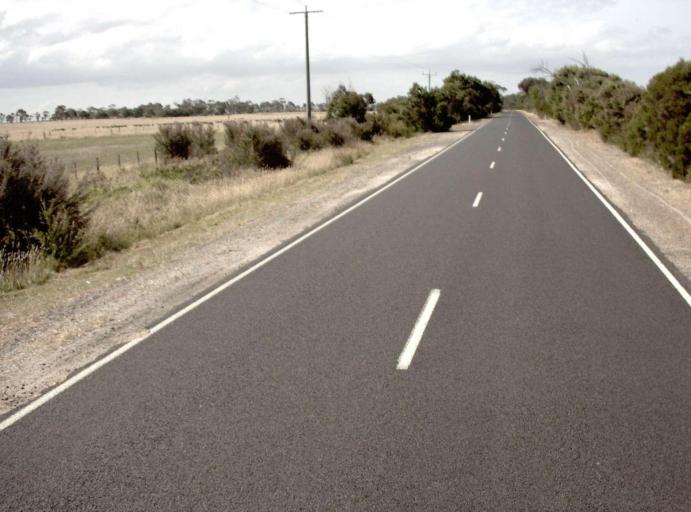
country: AU
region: Victoria
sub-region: Wellington
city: Sale
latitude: -38.3521
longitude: 147.1714
